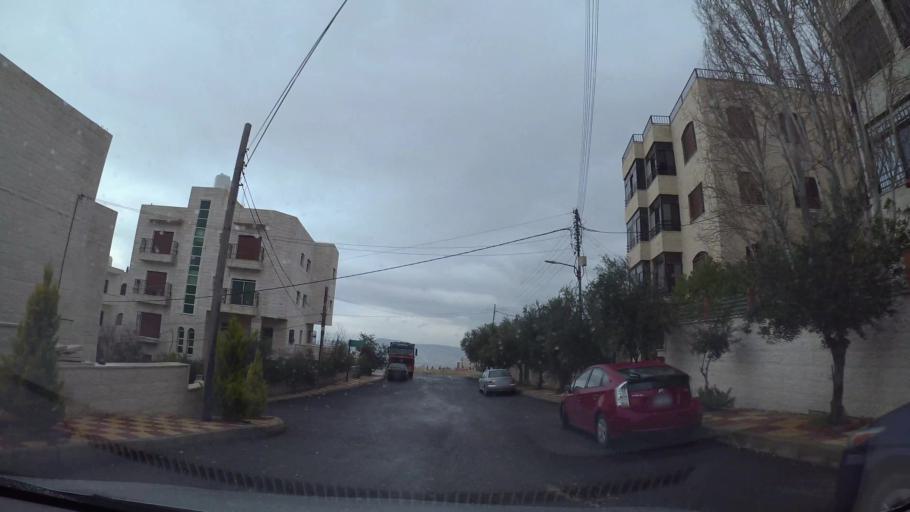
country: JO
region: Amman
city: Al Jubayhah
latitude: 32.0355
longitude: 35.8417
